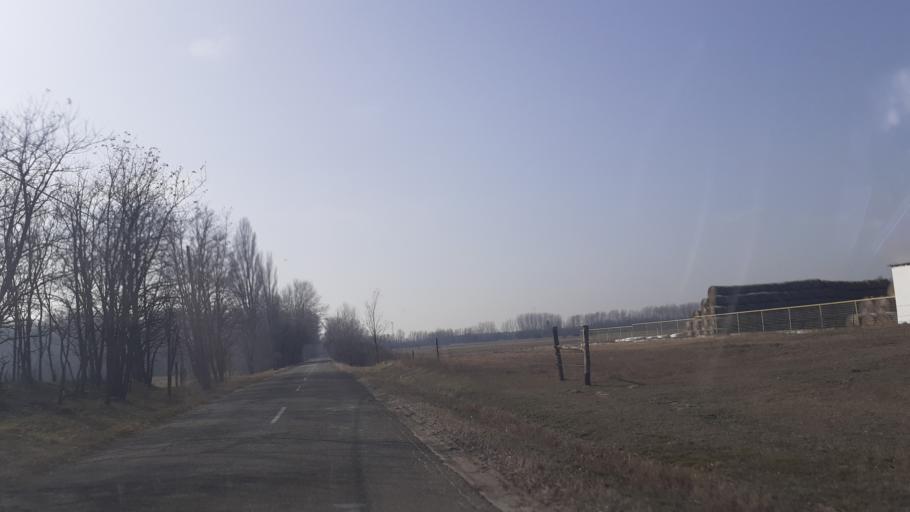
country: HU
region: Pest
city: Orkeny
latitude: 47.0658
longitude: 19.3493
